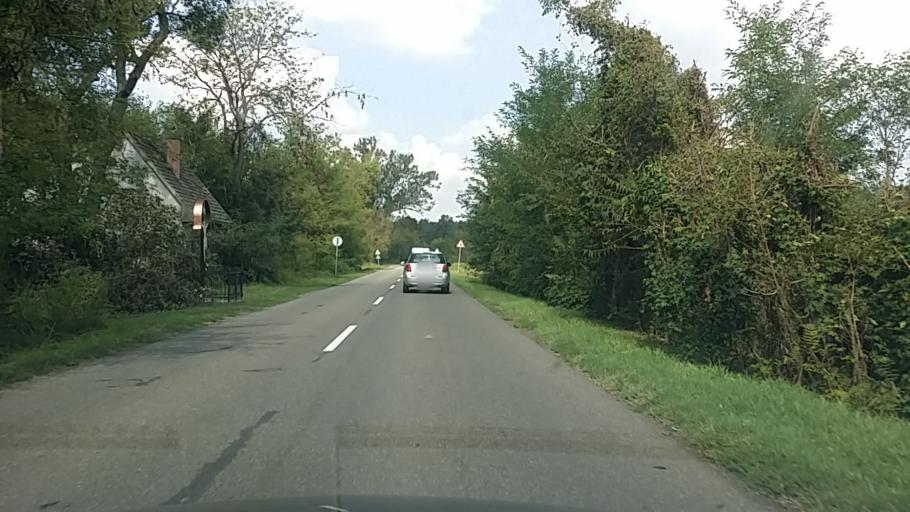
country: HU
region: Bacs-Kiskun
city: Tiszaalpar
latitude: 46.8378
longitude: 19.9779
